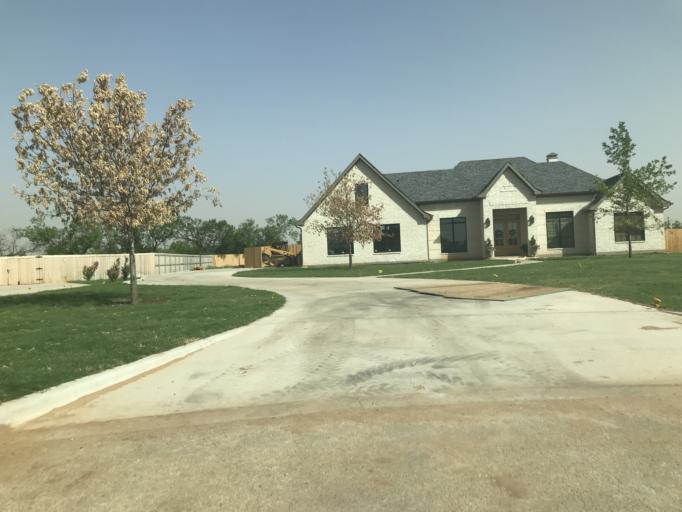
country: US
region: Texas
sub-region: Taylor County
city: Potosi
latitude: 32.3519
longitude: -99.7160
